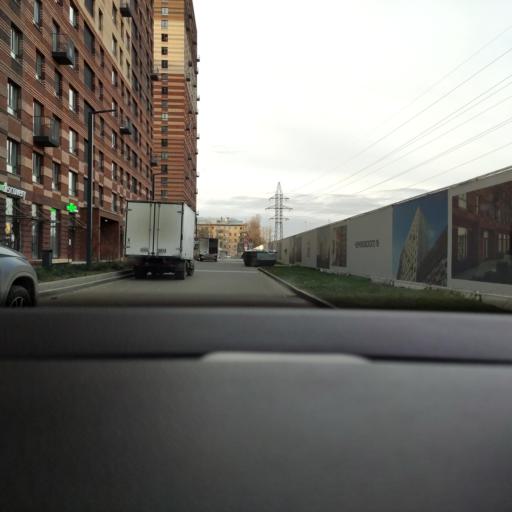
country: RU
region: Moskovskaya
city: Koptevo
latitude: 55.8090
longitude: 37.5418
